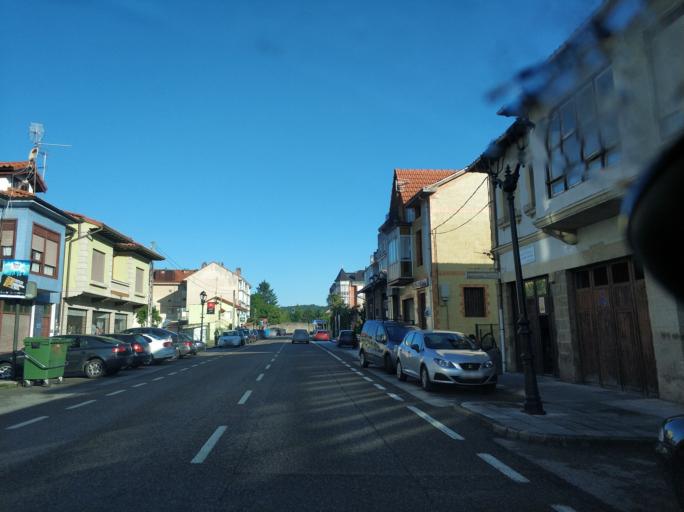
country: ES
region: Cantabria
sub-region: Provincia de Cantabria
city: Puente Viesgo
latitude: 43.3555
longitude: -3.9555
